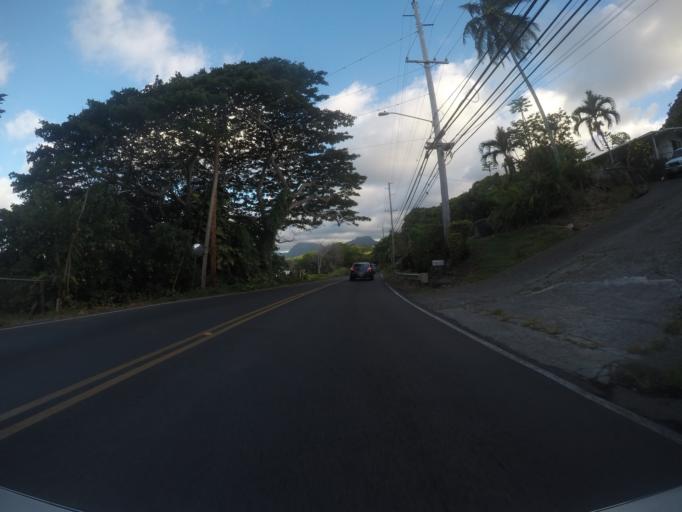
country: US
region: Hawaii
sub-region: Honolulu County
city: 'Ahuimanu
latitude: 21.4505
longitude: -157.8148
